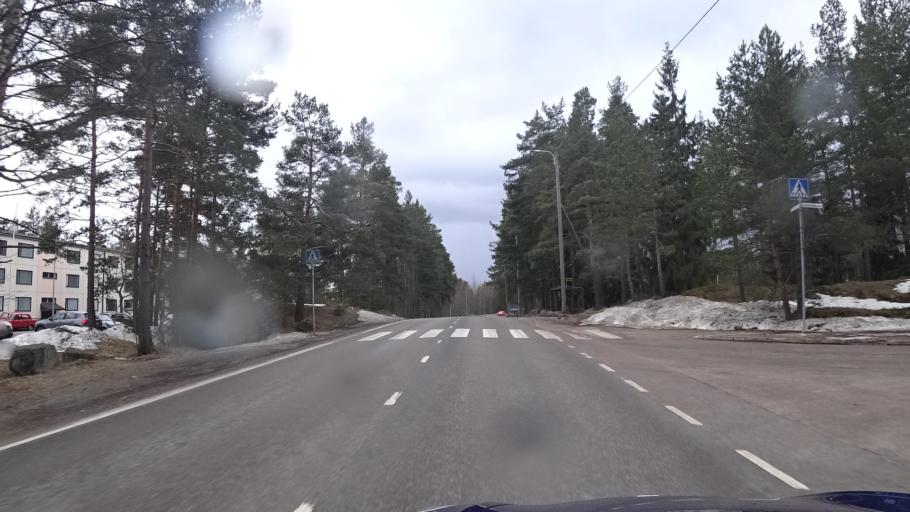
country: FI
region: Kymenlaakso
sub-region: Kotka-Hamina
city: Karhula
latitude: 60.5197
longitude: 26.8975
